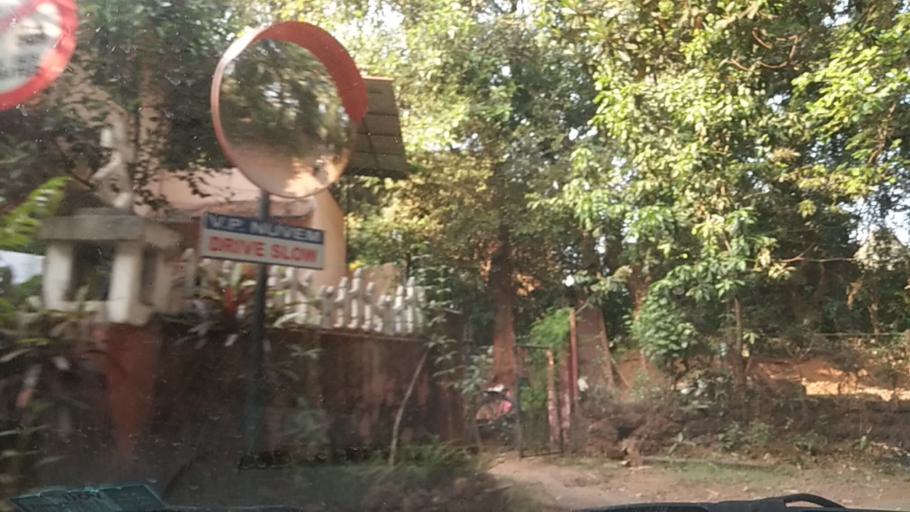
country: IN
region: Goa
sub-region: South Goa
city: Raia
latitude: 15.3218
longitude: 73.9321
